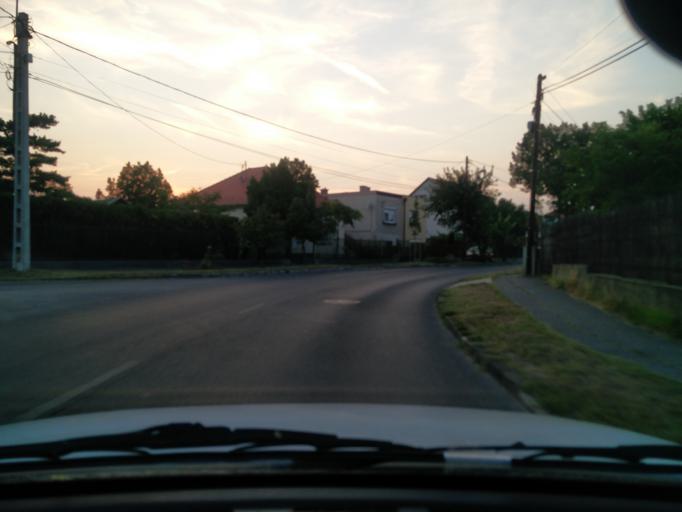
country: HU
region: Budapest
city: Budapest XXIII. keruelet
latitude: 47.3946
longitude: 19.1010
